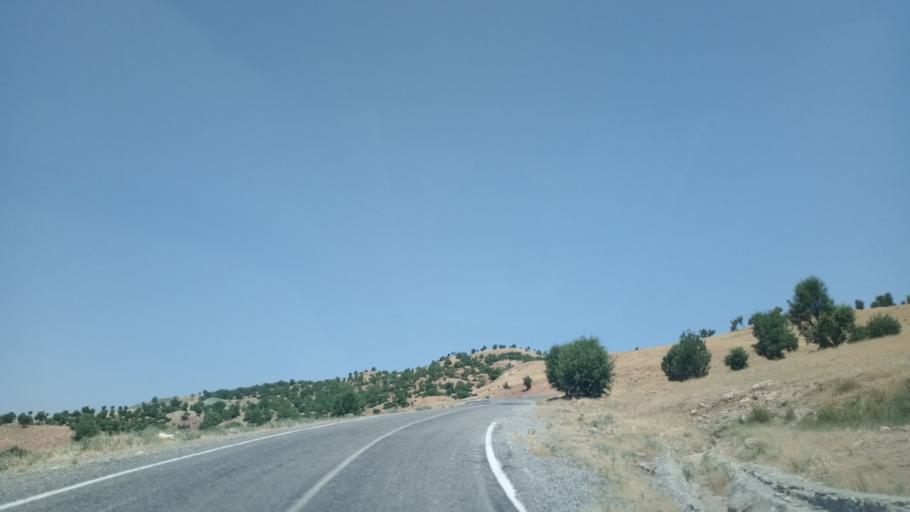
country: TR
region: Siirt
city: Dilektepe
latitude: 38.0616
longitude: 41.8321
